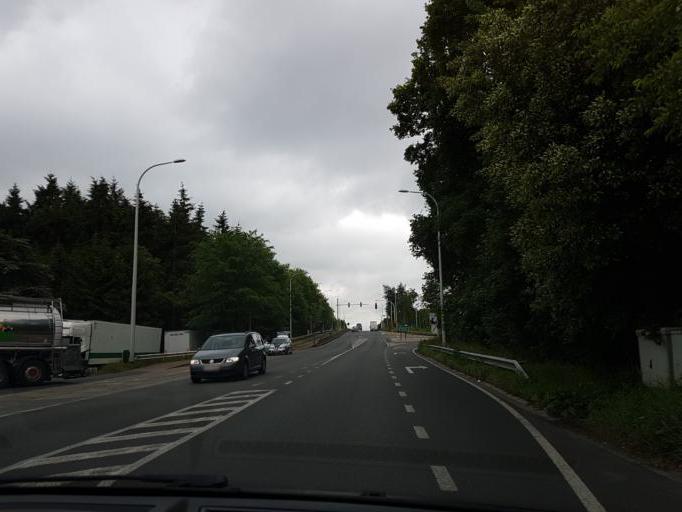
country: BE
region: Flanders
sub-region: Provincie West-Vlaanderen
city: Beernem
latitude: 51.1231
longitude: 3.3255
